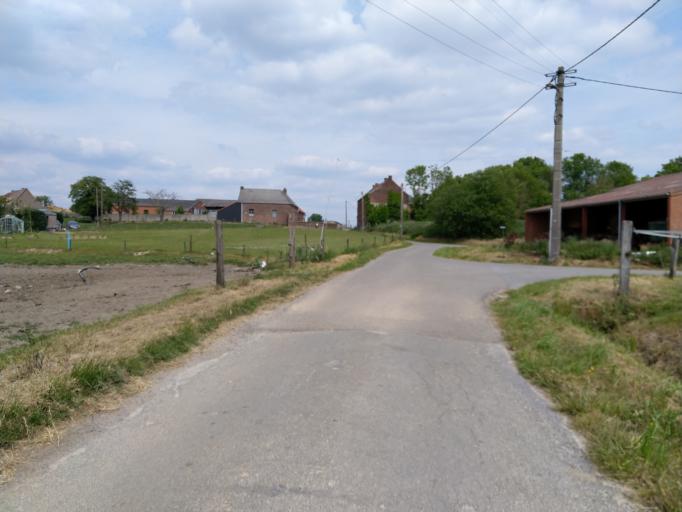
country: BE
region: Wallonia
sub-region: Province du Hainaut
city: Silly
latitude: 50.5915
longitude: 3.9665
